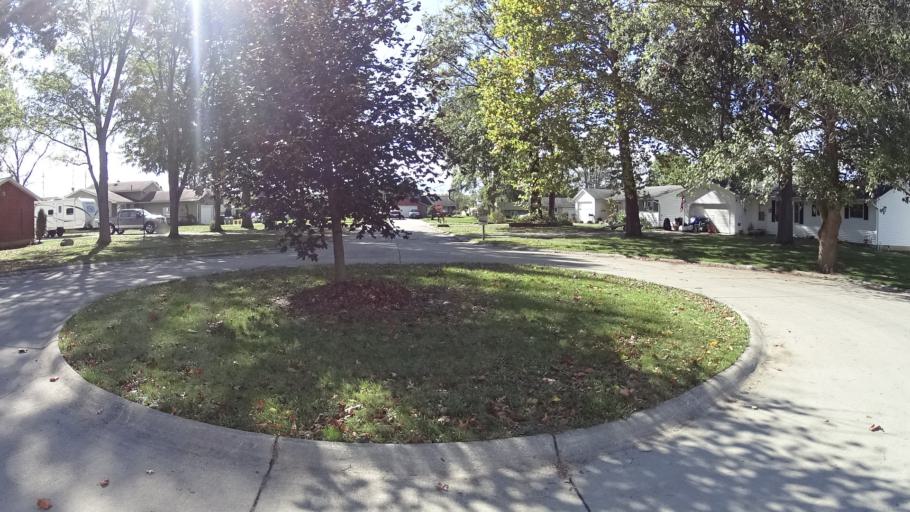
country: US
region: Ohio
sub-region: Lorain County
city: Grafton
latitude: 41.2815
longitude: -82.0612
